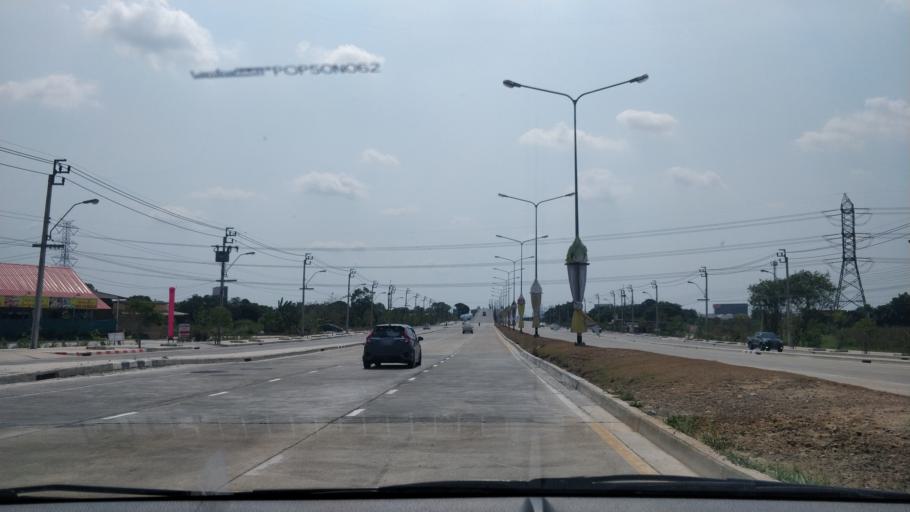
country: TH
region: Bangkok
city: Saphan Sung
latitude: 13.7537
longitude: 100.7092
